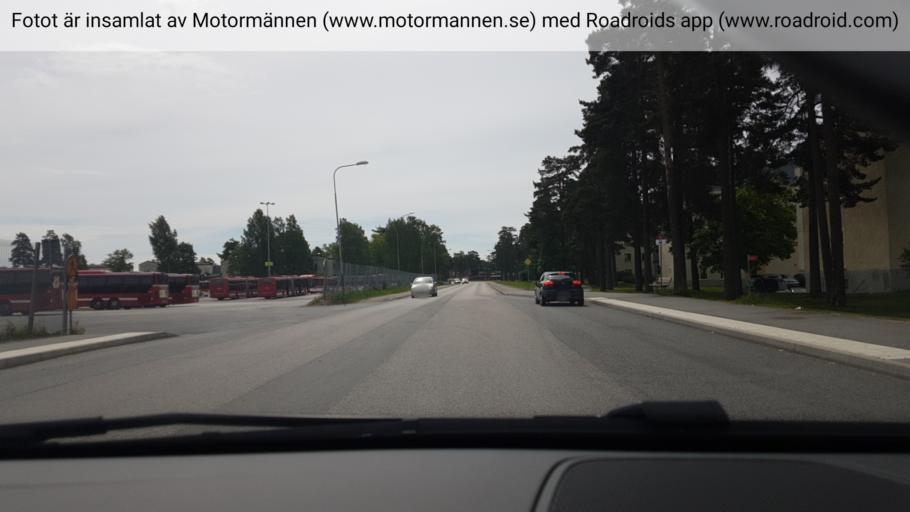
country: SE
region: Stockholm
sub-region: Haninge Kommun
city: Haninge
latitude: 59.1714
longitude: 18.1484
